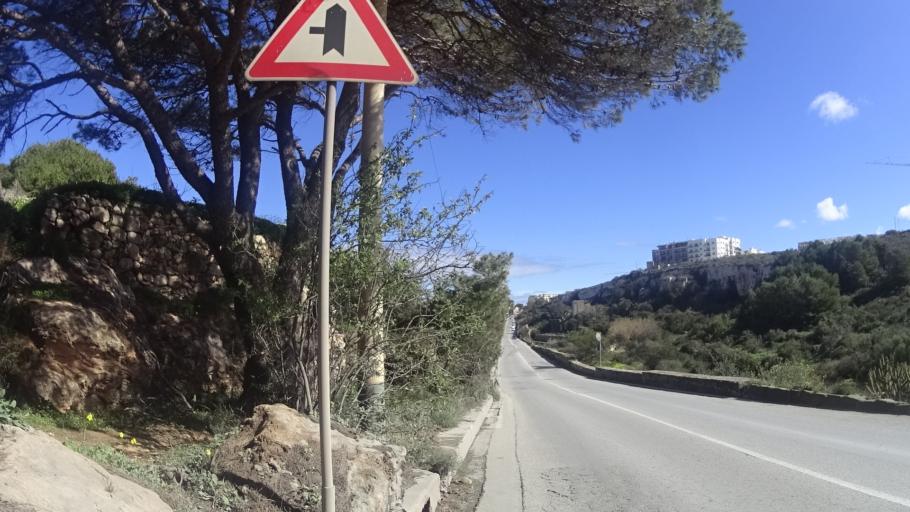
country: MT
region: Il-Mellieha
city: Mellieha
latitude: 35.9532
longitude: 14.3800
